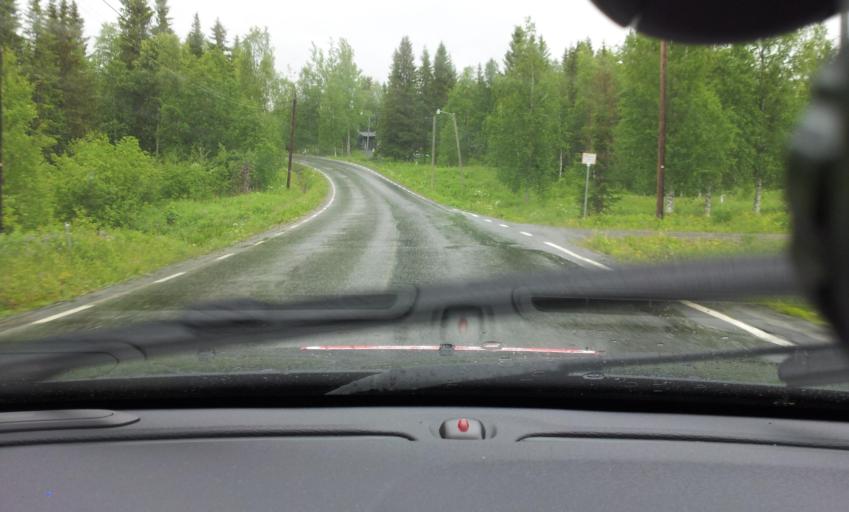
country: SE
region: Jaemtland
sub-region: Are Kommun
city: Are
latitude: 63.3112
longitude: 13.2087
